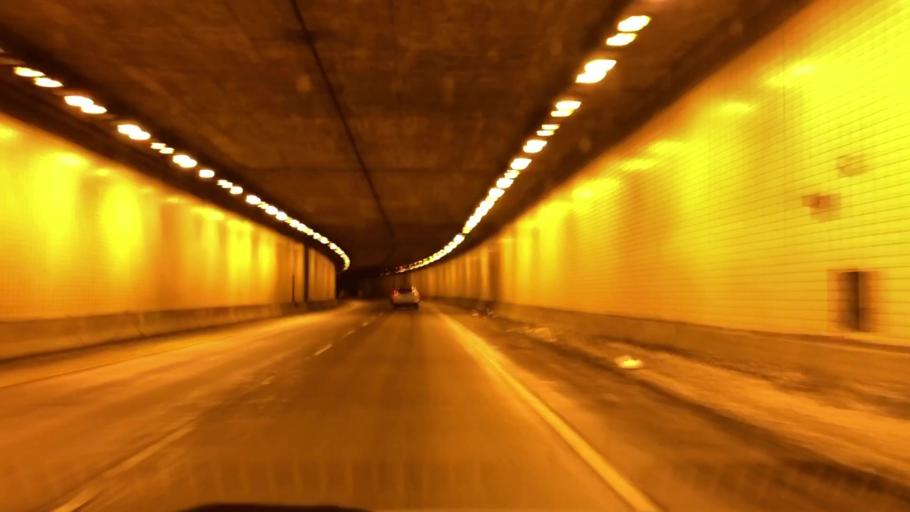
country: US
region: Minnesota
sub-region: Saint Louis County
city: Duluth
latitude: 46.7980
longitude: -92.0806
